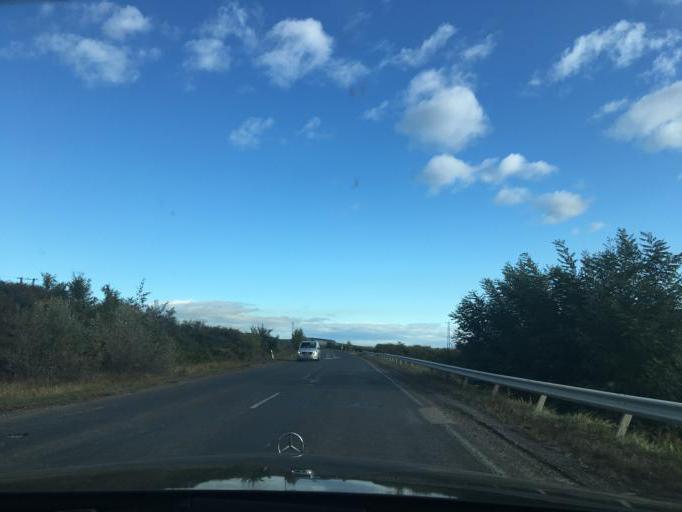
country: HU
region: Borsod-Abauj-Zemplen
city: Gonc
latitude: 48.4930
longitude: 21.2170
